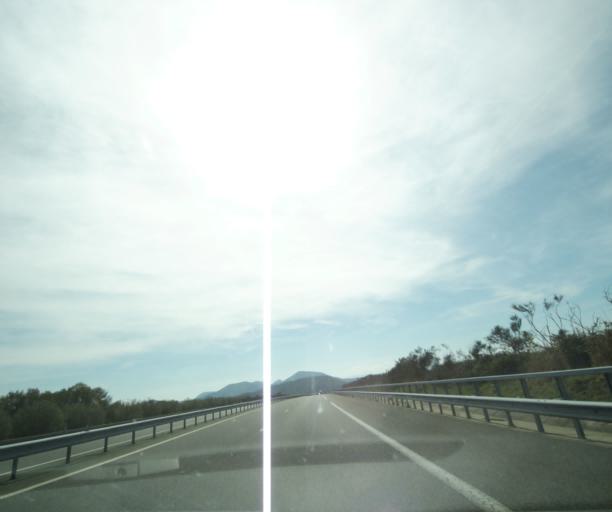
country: FR
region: Auvergne
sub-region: Departement du Puy-de-Dome
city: Manzat
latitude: 45.9213
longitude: 2.9603
